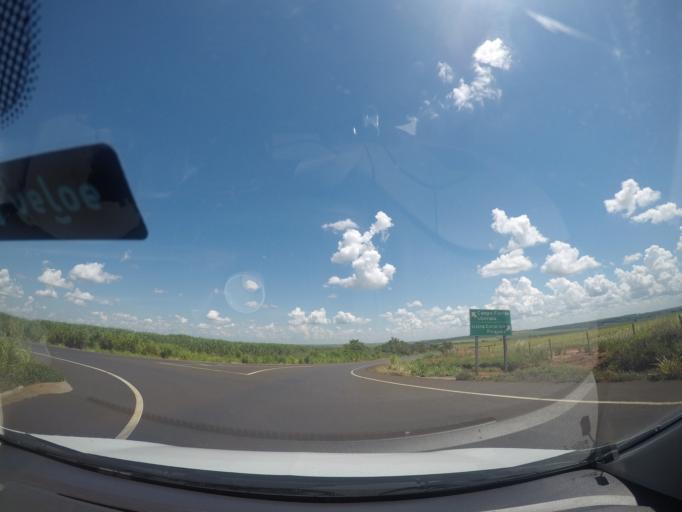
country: BR
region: Minas Gerais
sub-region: Frutal
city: Frutal
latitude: -19.7005
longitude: -48.7655
